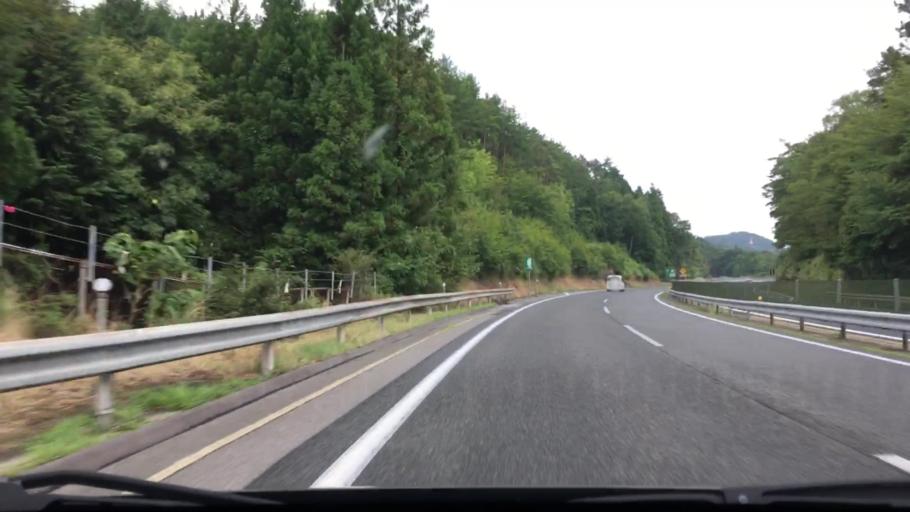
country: JP
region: Hiroshima
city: Miyoshi
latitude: 34.7038
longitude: 132.6121
